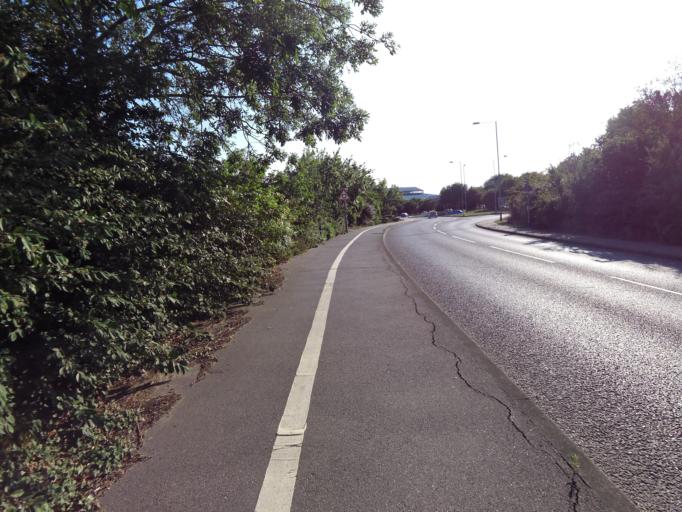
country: GB
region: England
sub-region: Essex
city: Chelmsford
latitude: 51.7475
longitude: 0.5068
